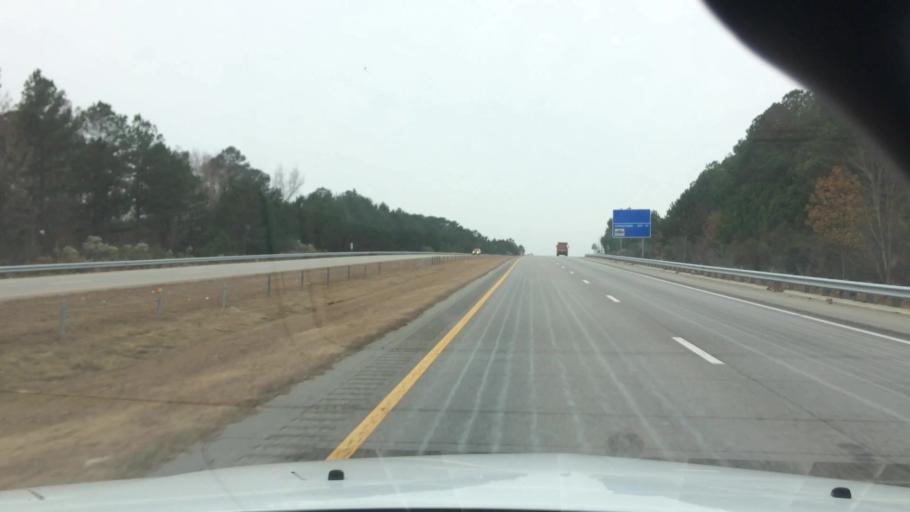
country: US
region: North Carolina
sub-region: Wilson County
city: Wilson
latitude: 35.6706
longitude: -77.8682
